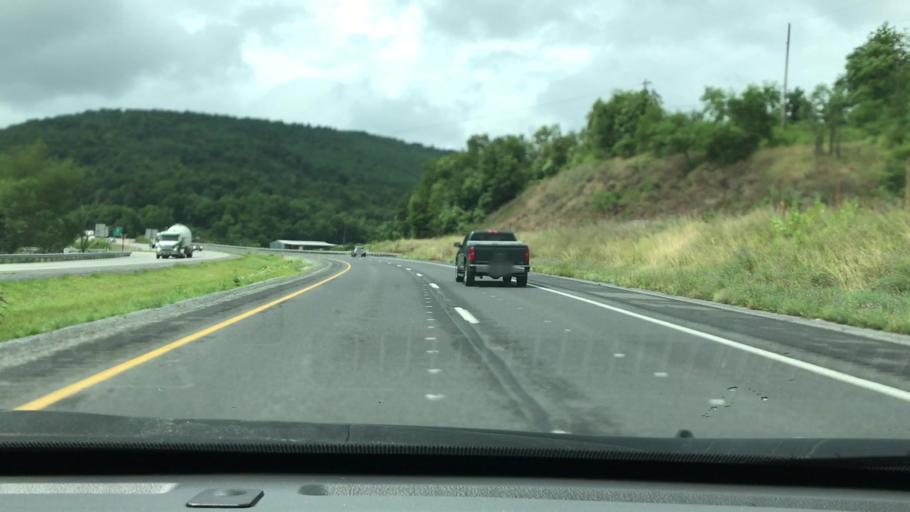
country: US
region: Pennsylvania
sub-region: Bedford County
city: Earlston
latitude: 39.9464
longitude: -78.2286
